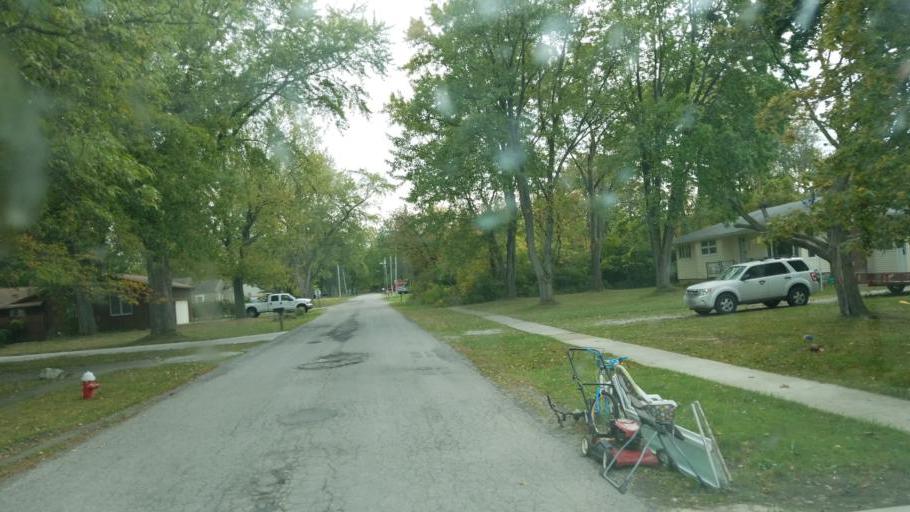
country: US
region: Ohio
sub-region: Lorain County
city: Sheffield Lake
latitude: 41.4835
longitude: -82.1232
